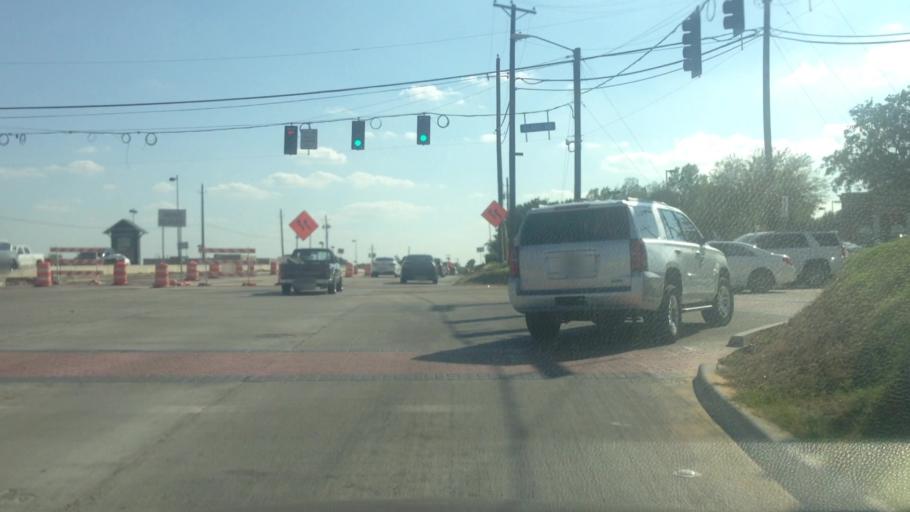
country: US
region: Texas
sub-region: Tarrant County
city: Colleyville
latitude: 32.8811
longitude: -97.1557
